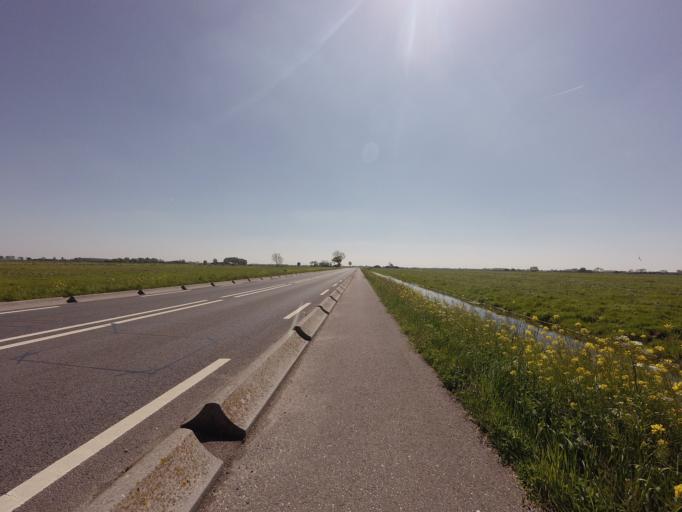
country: NL
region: South Holland
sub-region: Molenwaard
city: Liesveld
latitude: 51.9130
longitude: 4.7898
